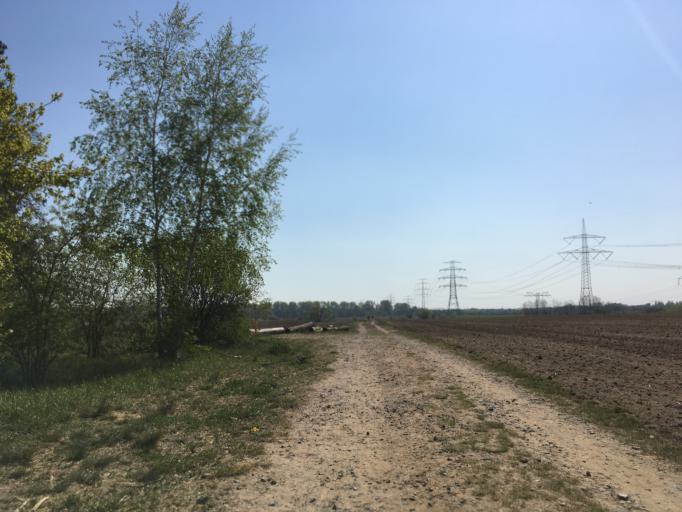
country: DE
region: Berlin
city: Buch
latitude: 52.6330
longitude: 13.4707
